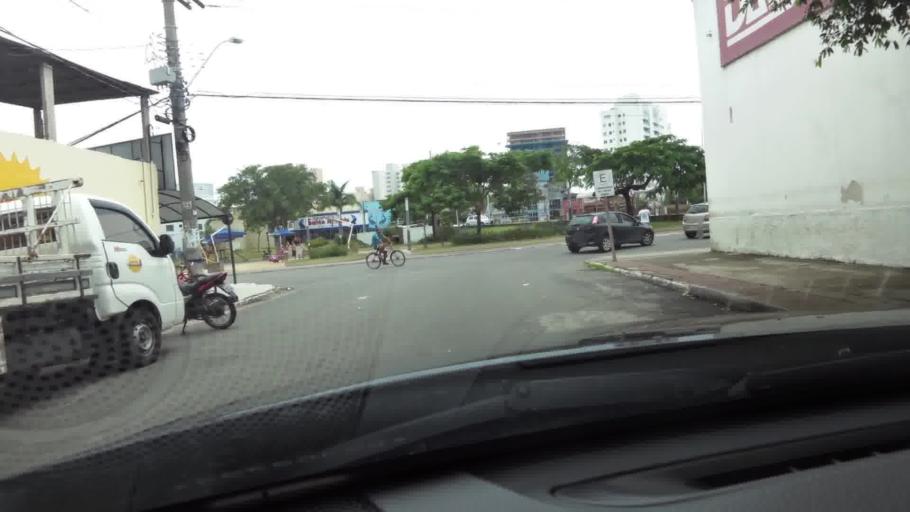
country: BR
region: Espirito Santo
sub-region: Guarapari
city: Guarapari
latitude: -20.6620
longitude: -40.4994
